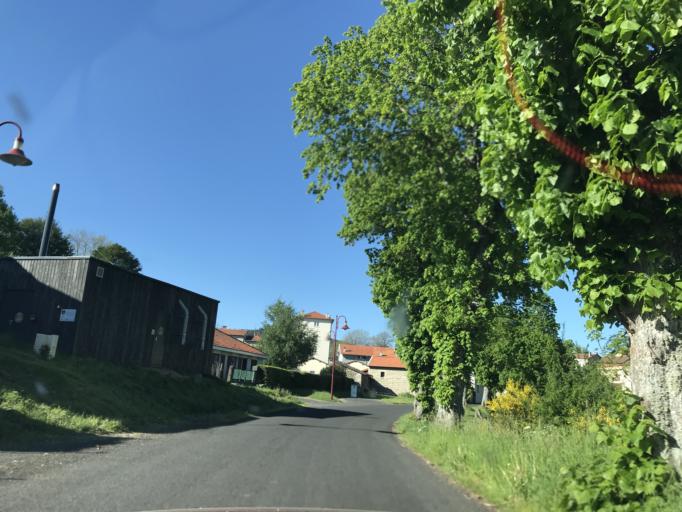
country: FR
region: Auvergne
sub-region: Departement du Puy-de-Dome
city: Cunlhat
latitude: 45.5760
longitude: 3.6341
